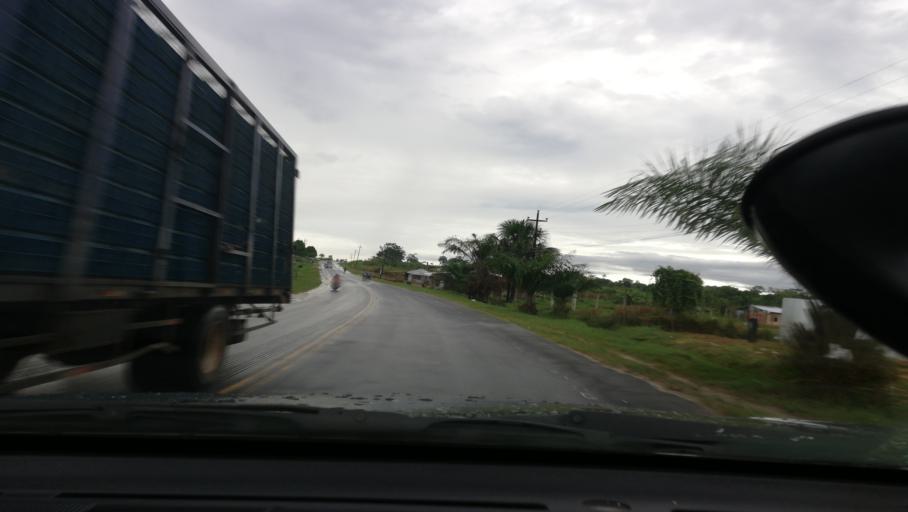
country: PE
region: Loreto
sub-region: Provincia de Maynas
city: Iquitos
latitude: -3.8513
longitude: -73.3386
